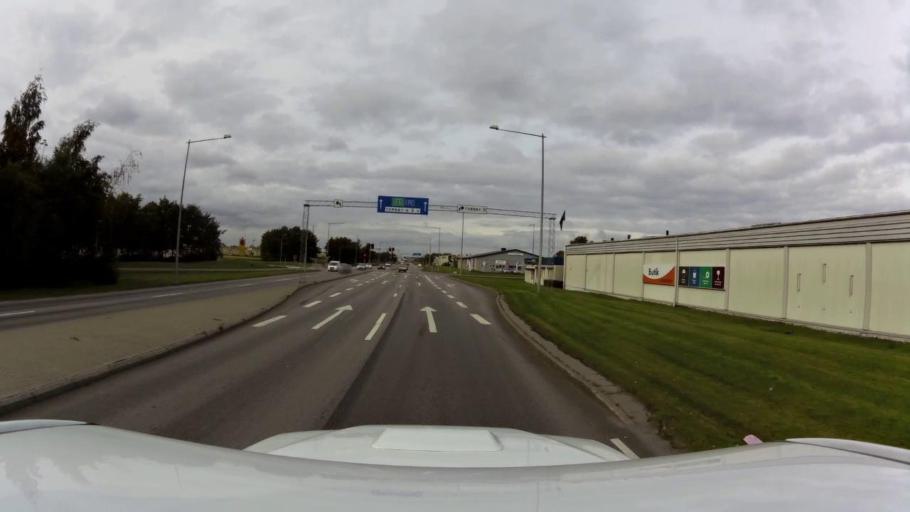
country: SE
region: OEstergoetland
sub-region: Linkopings Kommun
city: Linkoping
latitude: 58.4270
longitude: 15.6126
